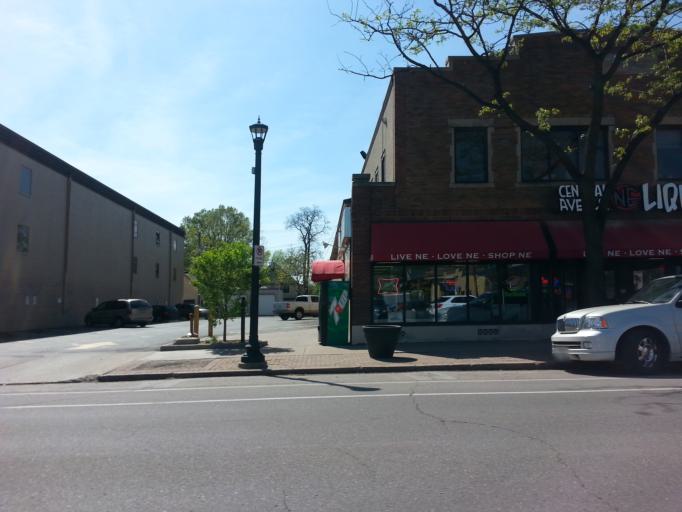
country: US
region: Minnesota
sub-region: Hennepin County
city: Saint Anthony
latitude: 45.0145
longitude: -93.2473
